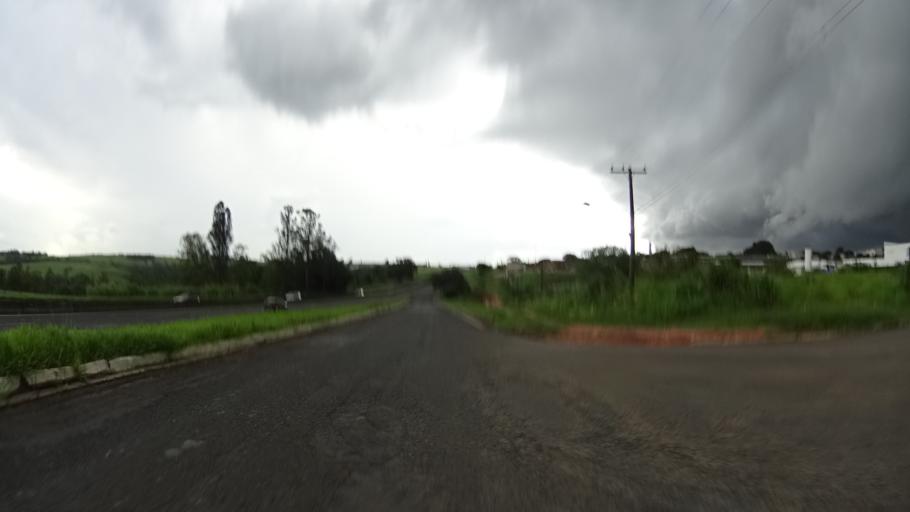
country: BR
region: Sao Paulo
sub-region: Marilia
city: Marilia
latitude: -22.2229
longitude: -49.8837
